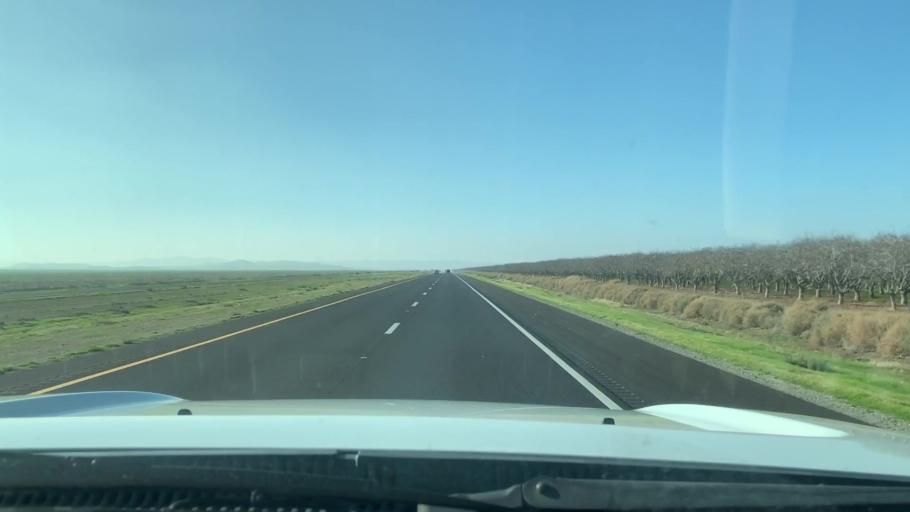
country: US
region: California
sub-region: Kern County
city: Lost Hills
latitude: 35.6148
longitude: -119.9098
